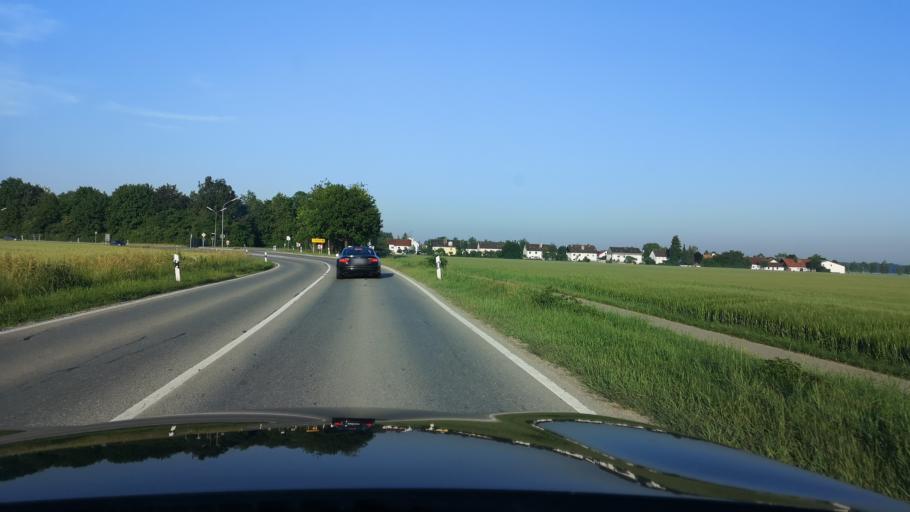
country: DE
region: Bavaria
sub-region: Upper Bavaria
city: Kirchheim bei Muenchen
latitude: 48.1815
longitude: 11.7638
